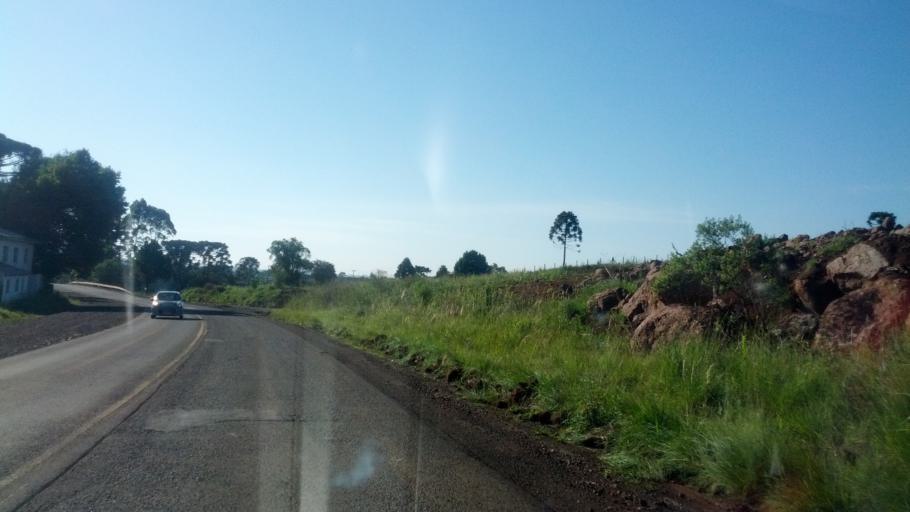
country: BR
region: Santa Catarina
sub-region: Lages
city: Lages
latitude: -27.9374
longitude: -50.5137
